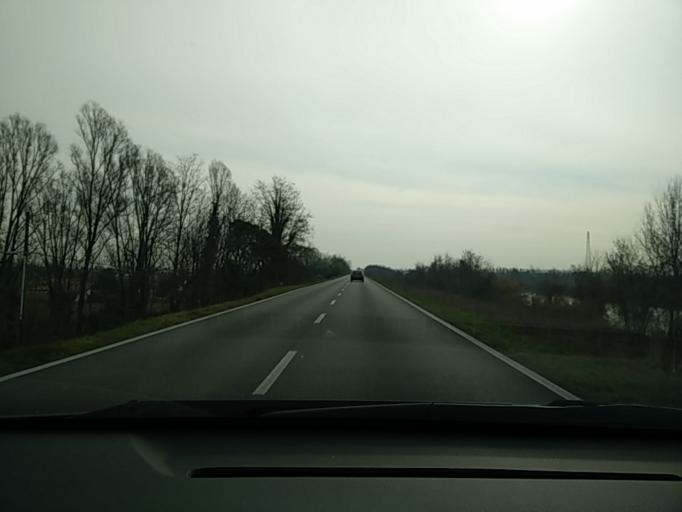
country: IT
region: Veneto
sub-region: Provincia di Venezia
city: San Dona di Piave
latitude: 45.6146
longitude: 12.5793
